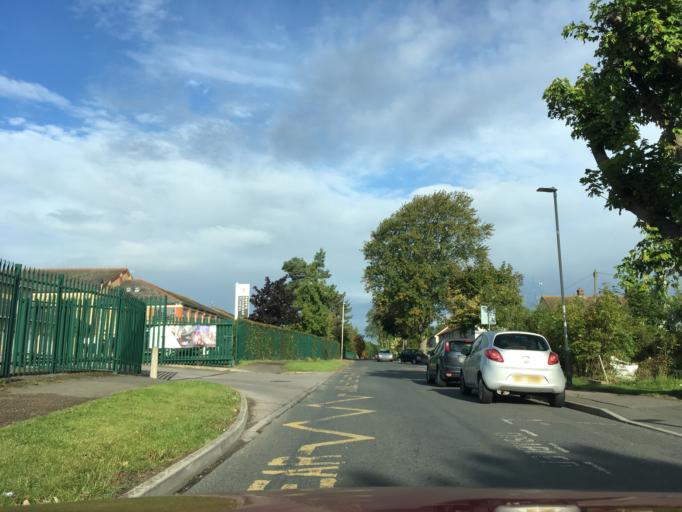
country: GB
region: England
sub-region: Gloucestershire
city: Uckington
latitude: 51.9066
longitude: -2.1148
